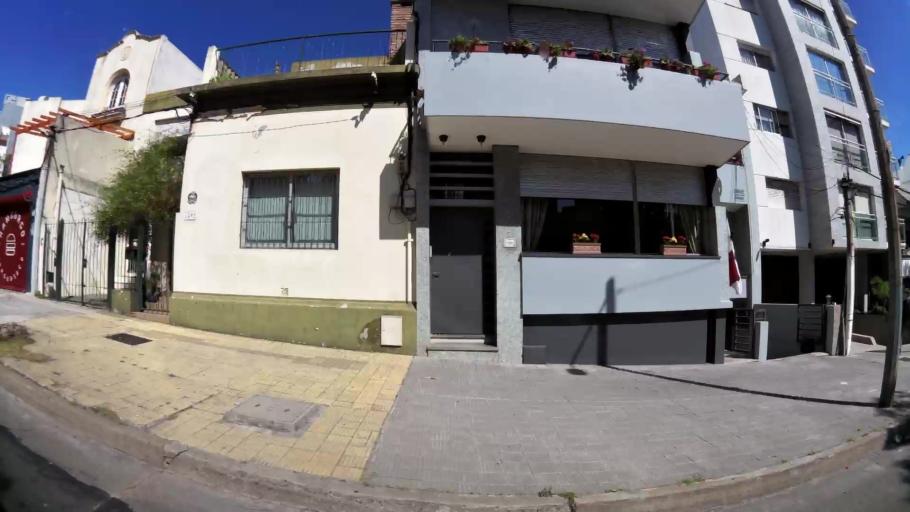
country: UY
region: Montevideo
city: Montevideo
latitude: -34.9067
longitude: -56.1399
